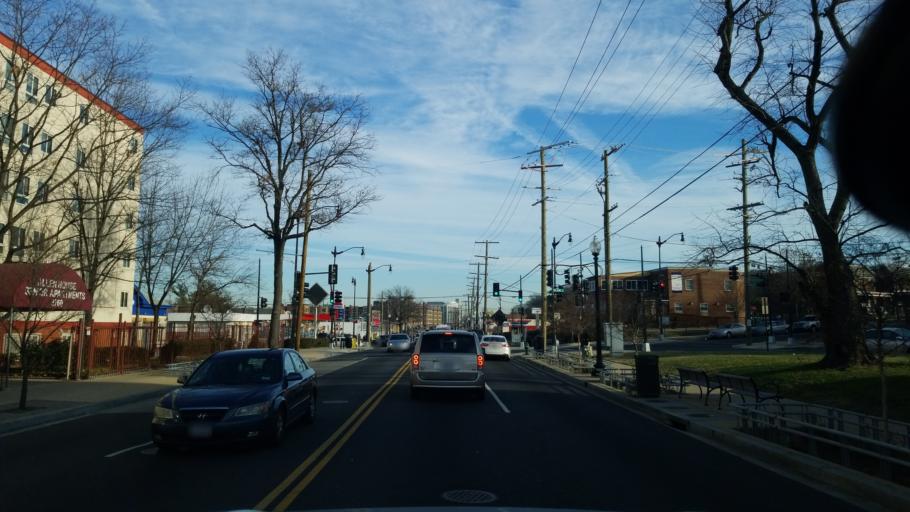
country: US
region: Maryland
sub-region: Prince George's County
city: Capitol Heights
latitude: 38.8915
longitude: -76.9518
